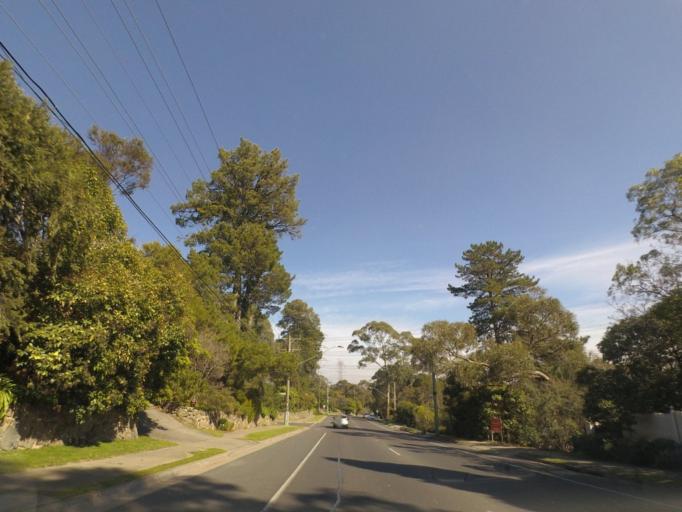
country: AU
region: Victoria
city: Mitcham
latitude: -37.8095
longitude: 145.2177
